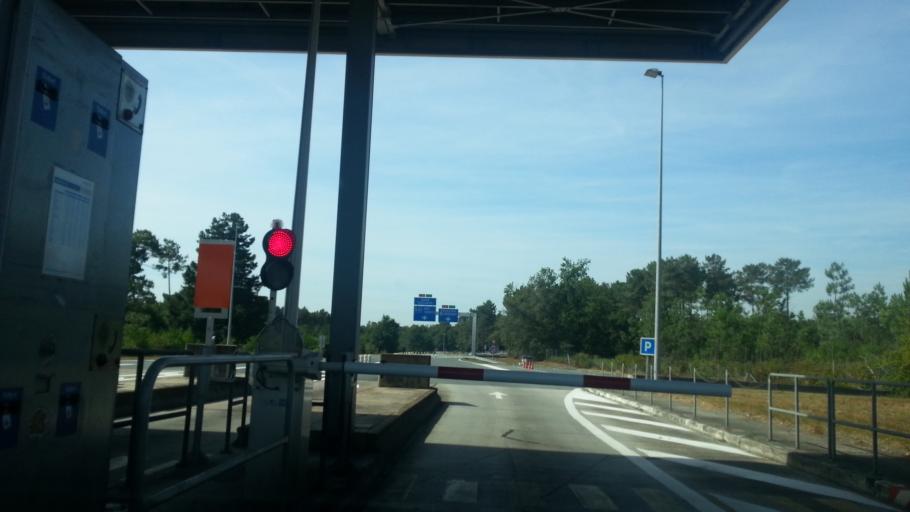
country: FR
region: Aquitaine
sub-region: Departement de la Gironde
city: Illats
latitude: 44.6076
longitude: -0.3669
